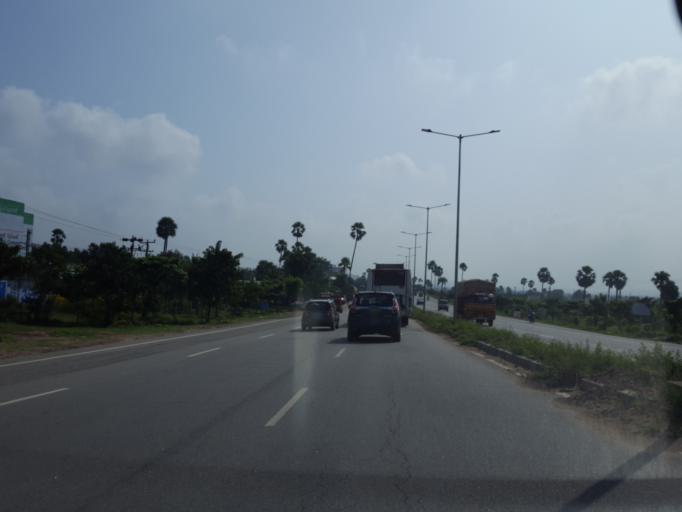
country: IN
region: Telangana
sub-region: Rangareddi
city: Lal Bahadur Nagar
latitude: 17.3095
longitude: 78.6933
